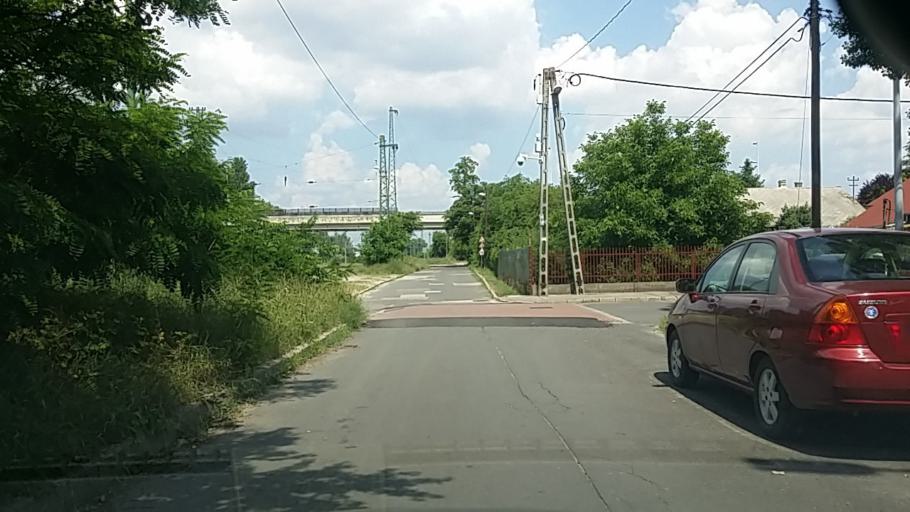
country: HU
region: Budapest
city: Budapest XVI. keruelet
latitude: 47.5185
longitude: 19.1488
